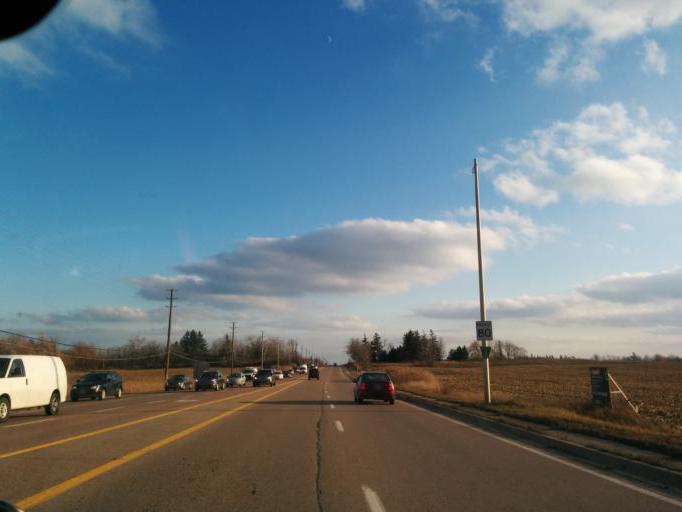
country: CA
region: Ontario
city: Oakville
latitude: 43.5012
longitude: -79.7375
